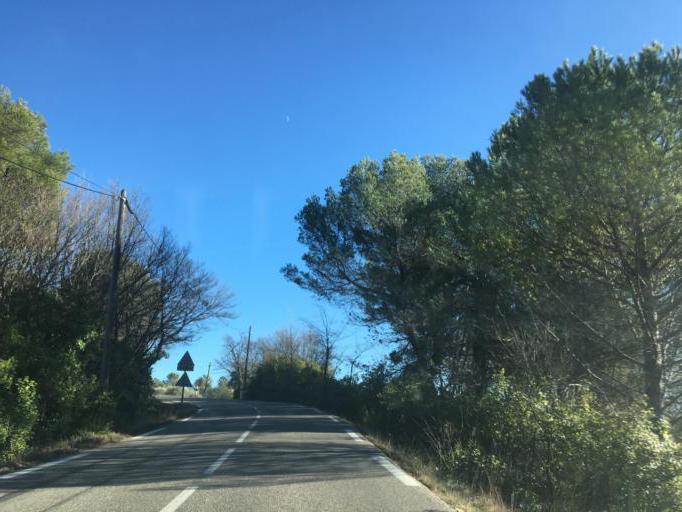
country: FR
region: Provence-Alpes-Cote d'Azur
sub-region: Departement du Var
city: Barjols
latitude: 43.5922
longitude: 5.9720
